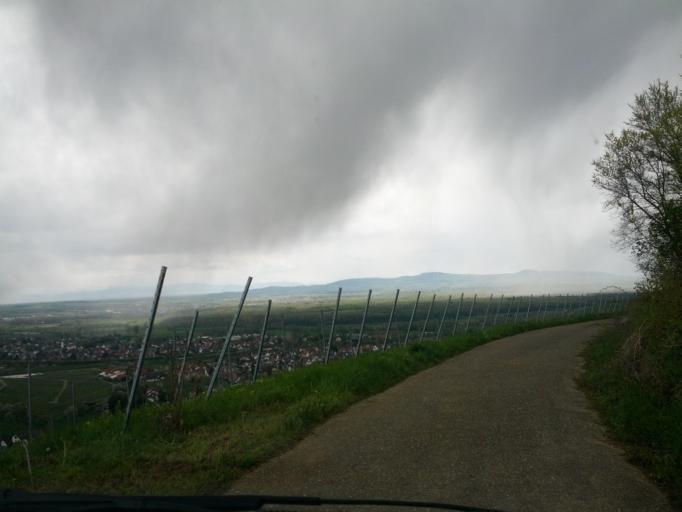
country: DE
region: Baden-Wuerttemberg
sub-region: Freiburg Region
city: Ebringen
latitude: 47.9485
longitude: 7.7821
